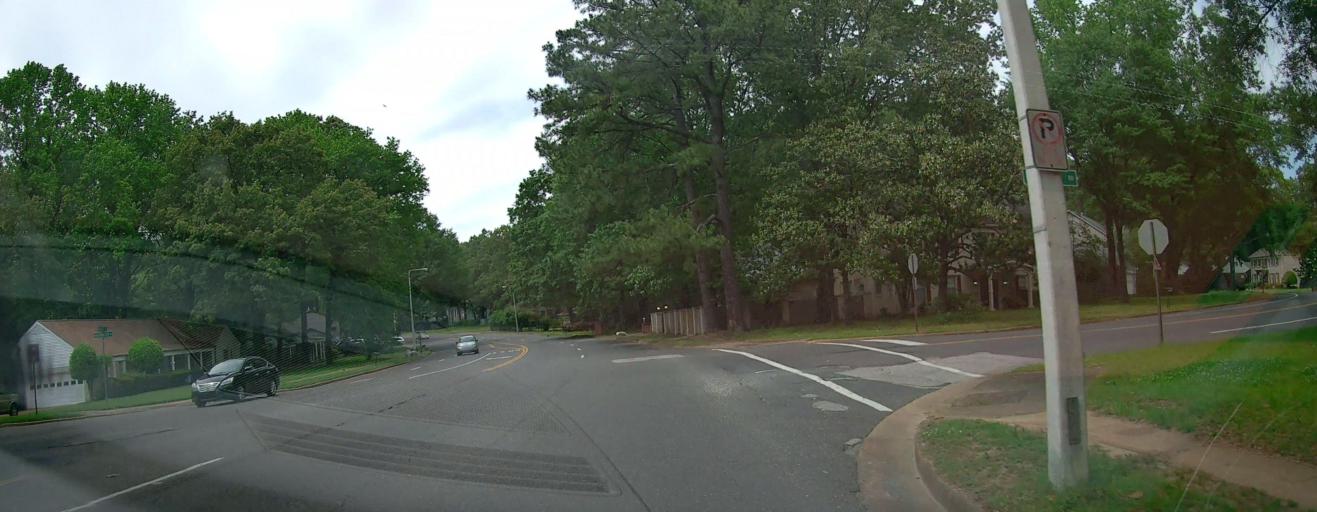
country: US
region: Tennessee
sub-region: Shelby County
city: Germantown
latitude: 35.0833
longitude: -89.8523
